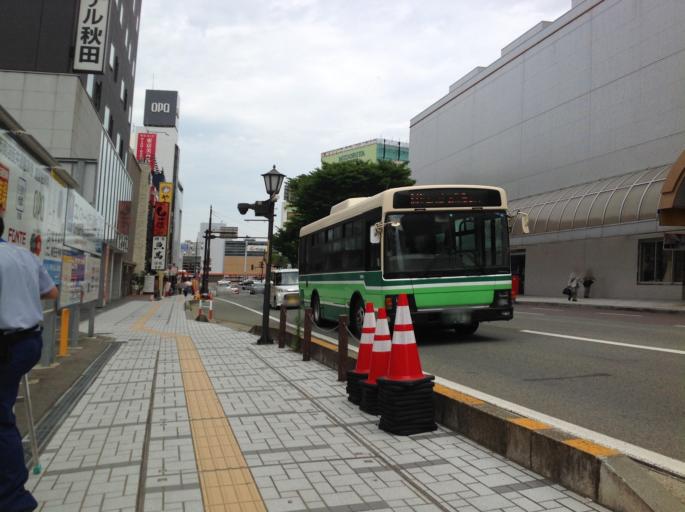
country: JP
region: Akita
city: Akita
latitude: 39.7180
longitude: 140.1266
